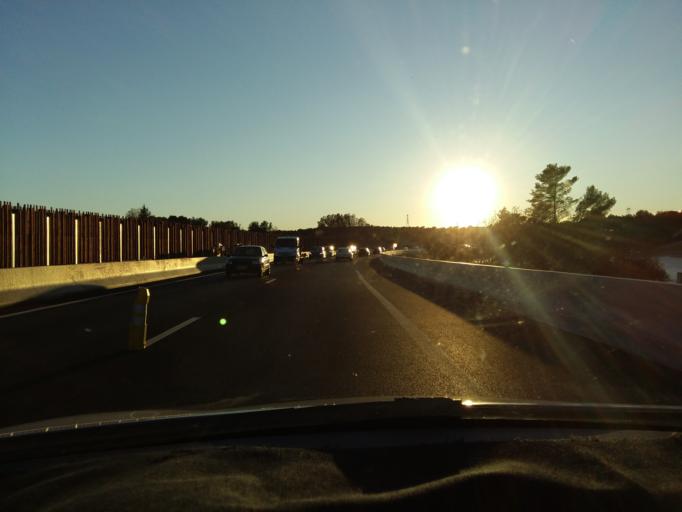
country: FR
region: Provence-Alpes-Cote d'Azur
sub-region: Departement des Bouches-du-Rhone
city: Cabries
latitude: 43.4581
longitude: 5.3308
